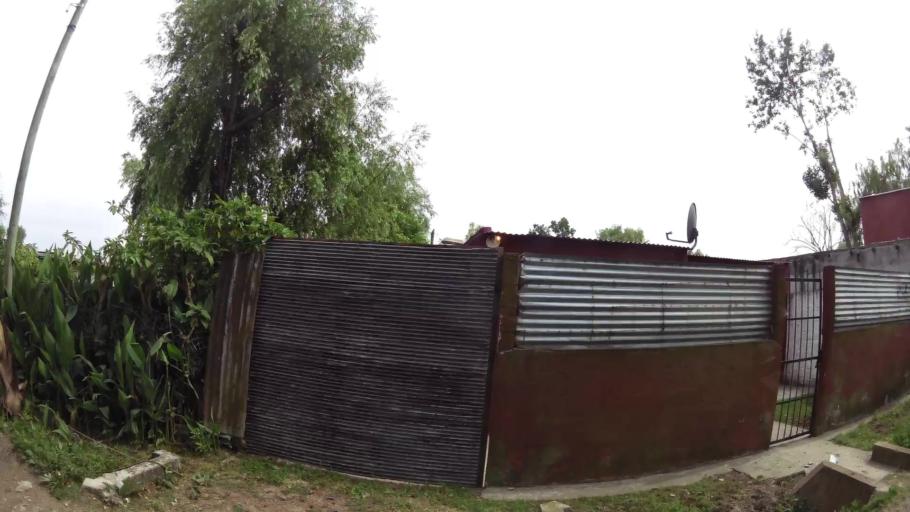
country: UY
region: Montevideo
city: Montevideo
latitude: -34.8345
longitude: -56.1769
